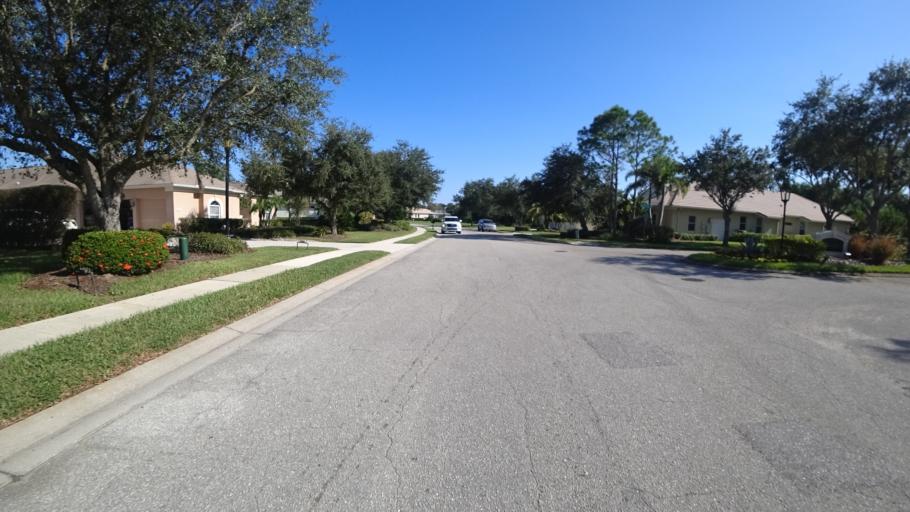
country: US
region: Florida
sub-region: Sarasota County
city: The Meadows
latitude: 27.4059
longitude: -82.4412
